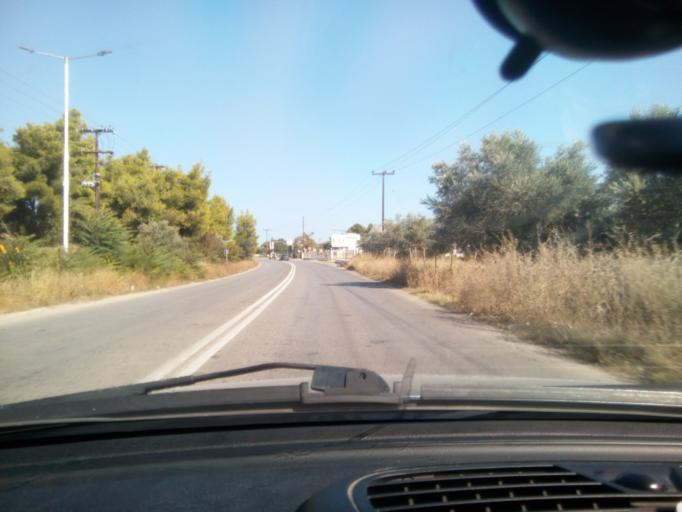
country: GR
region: Central Greece
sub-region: Nomos Evvoias
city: Vasilikon
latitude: 38.4164
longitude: 23.6954
